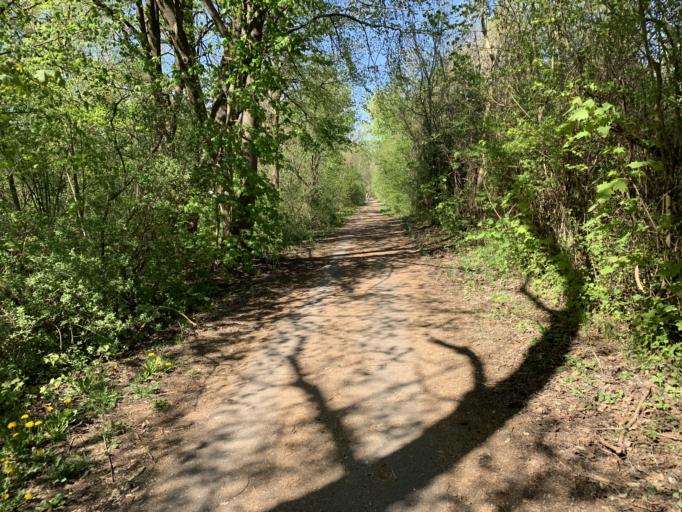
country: DE
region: Bavaria
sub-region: Swabia
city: Gersthofen
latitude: 48.4286
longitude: 10.8915
